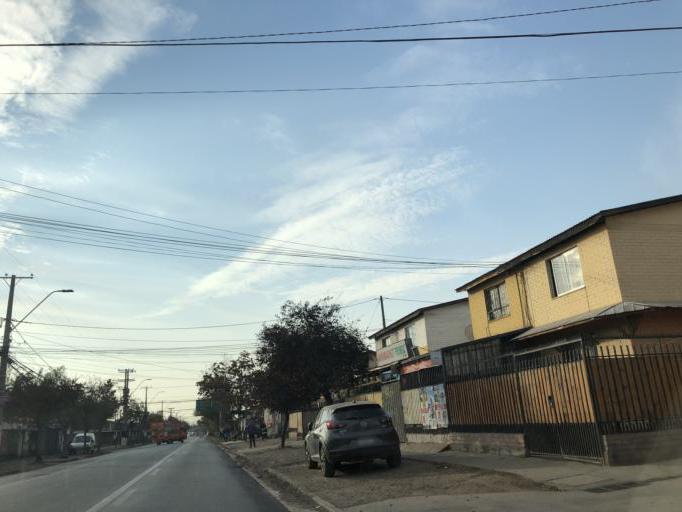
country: CL
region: Santiago Metropolitan
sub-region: Provincia de Cordillera
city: Puente Alto
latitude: -33.6001
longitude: -70.5656
